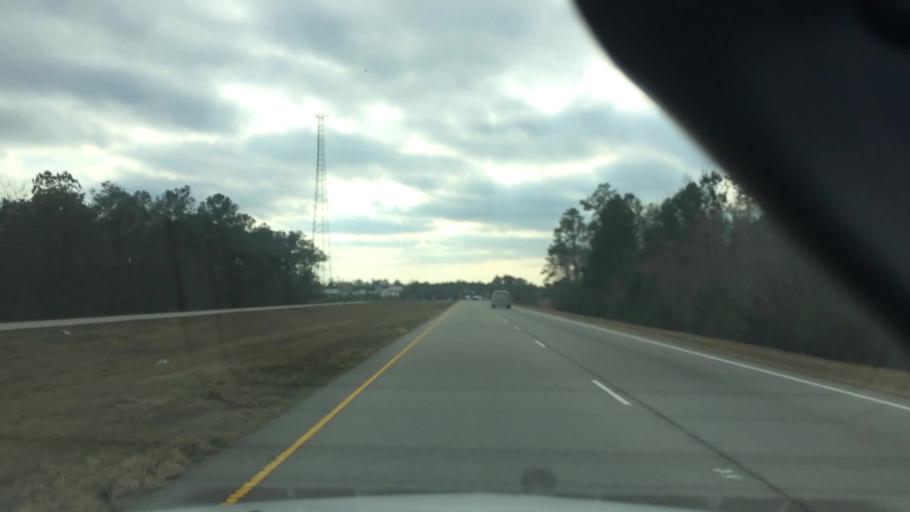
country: US
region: North Carolina
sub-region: Brunswick County
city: Shallotte
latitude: 33.9667
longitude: -78.4139
